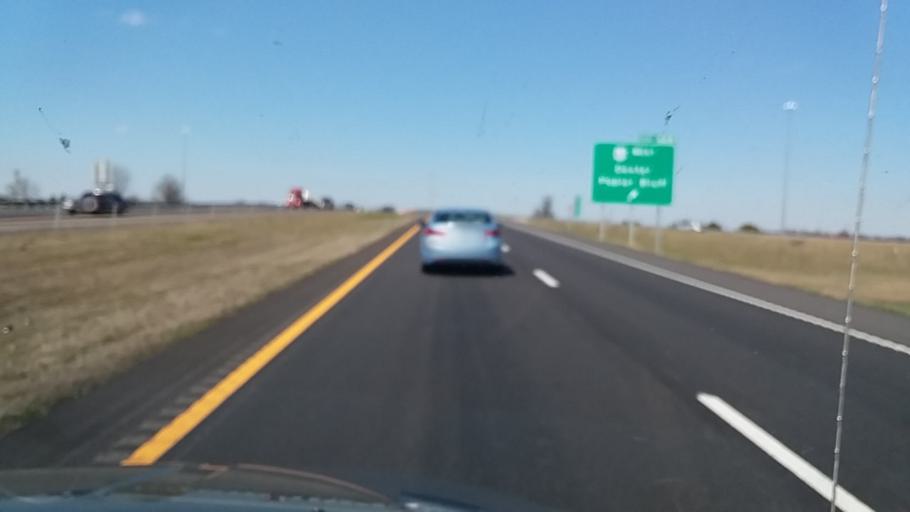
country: US
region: Missouri
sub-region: Scott County
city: Sikeston
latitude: 36.8713
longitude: -89.5329
